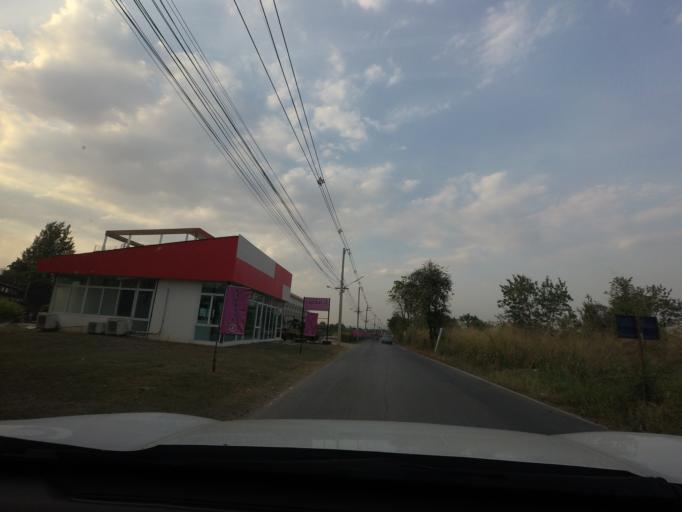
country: TH
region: Nakhon Ratchasima
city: Pak Chong
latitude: 14.5947
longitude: 101.4461
